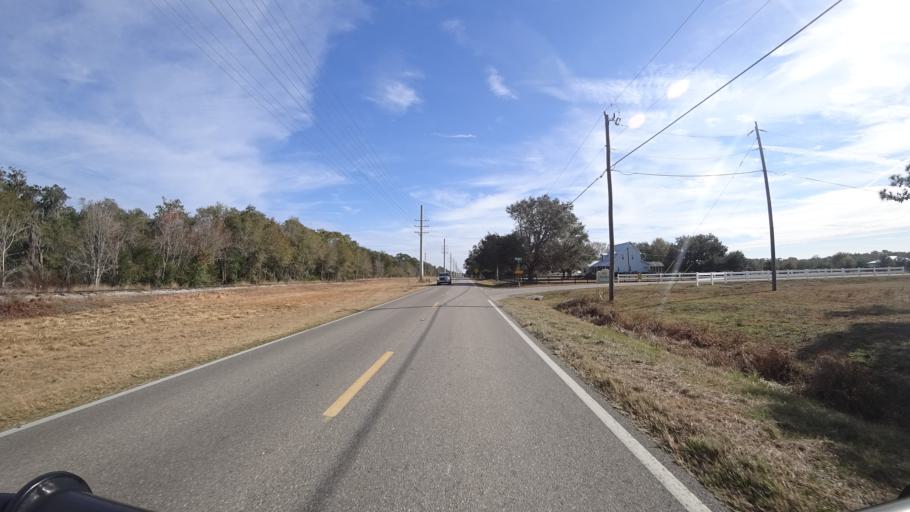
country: US
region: Florida
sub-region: Manatee County
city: Ellenton
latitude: 27.5800
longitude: -82.4556
